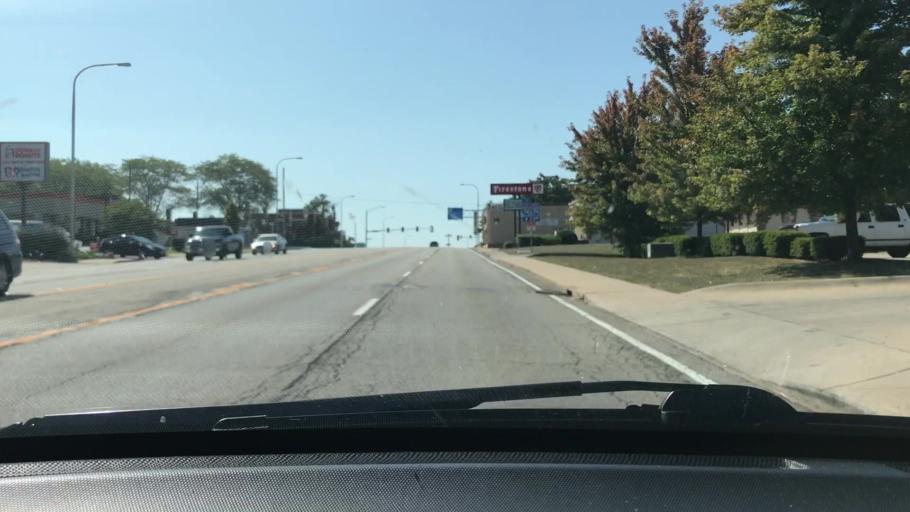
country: US
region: Illinois
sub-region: Peoria County
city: North Peoria
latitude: 40.7073
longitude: -89.5941
